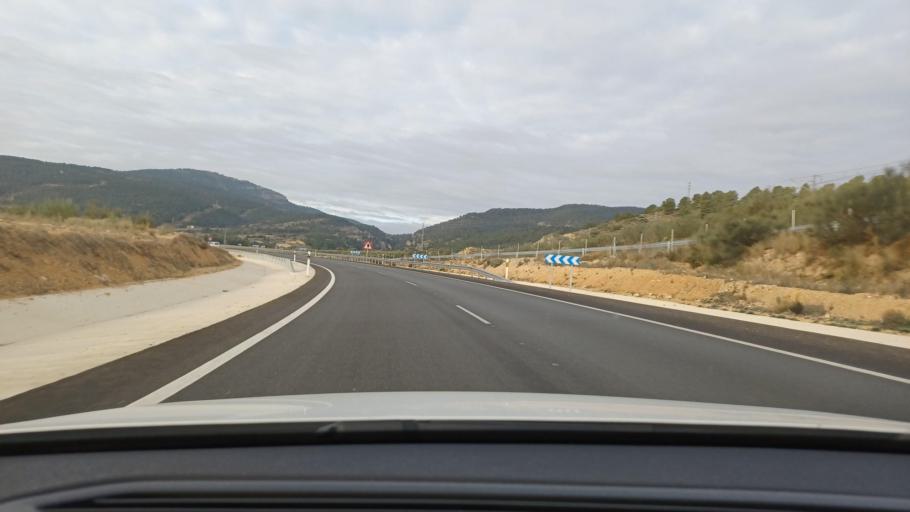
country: ES
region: Valencia
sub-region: Provincia de Valencia
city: La Font de la Figuera
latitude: 38.8306
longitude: -0.8891
